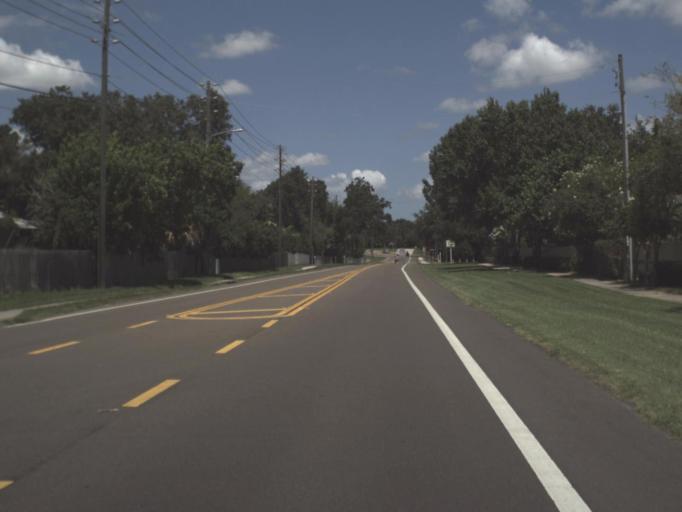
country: US
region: Florida
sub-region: Pinellas County
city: Oldsmar
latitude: 28.0219
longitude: -82.6887
